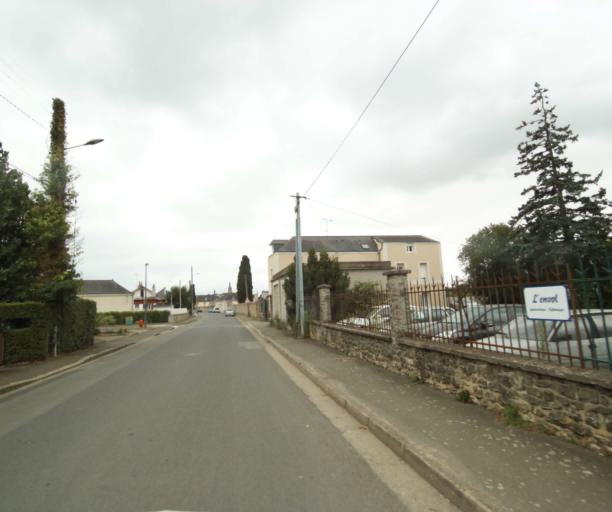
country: FR
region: Pays de la Loire
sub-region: Departement de la Sarthe
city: Sable-sur-Sarthe
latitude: 47.8420
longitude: -0.3219
